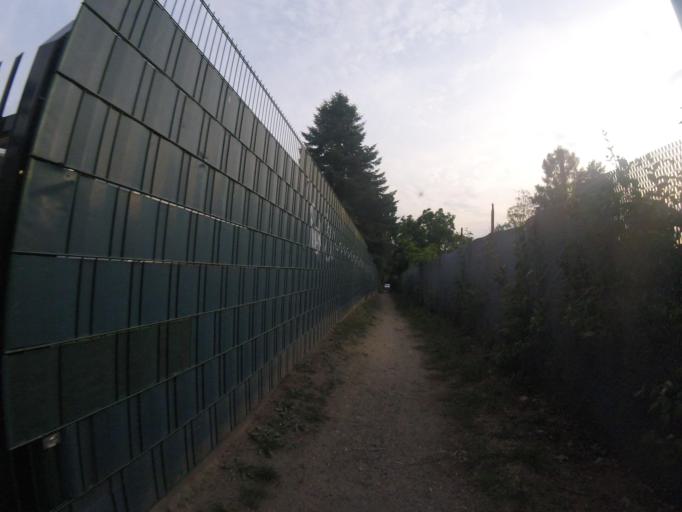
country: DE
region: Brandenburg
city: Zeuthen
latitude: 52.3433
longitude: 13.6146
